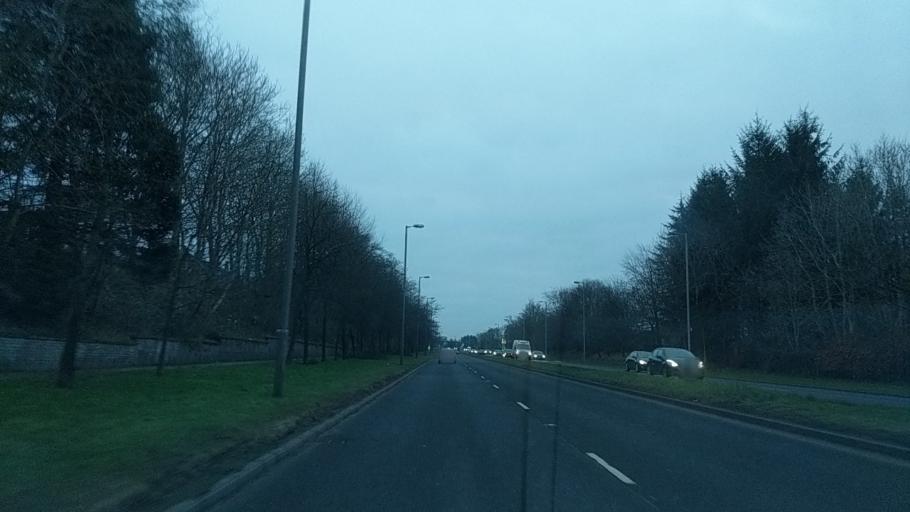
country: GB
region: Scotland
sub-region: South Lanarkshire
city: East Kilbride
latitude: 55.7707
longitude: -4.1644
